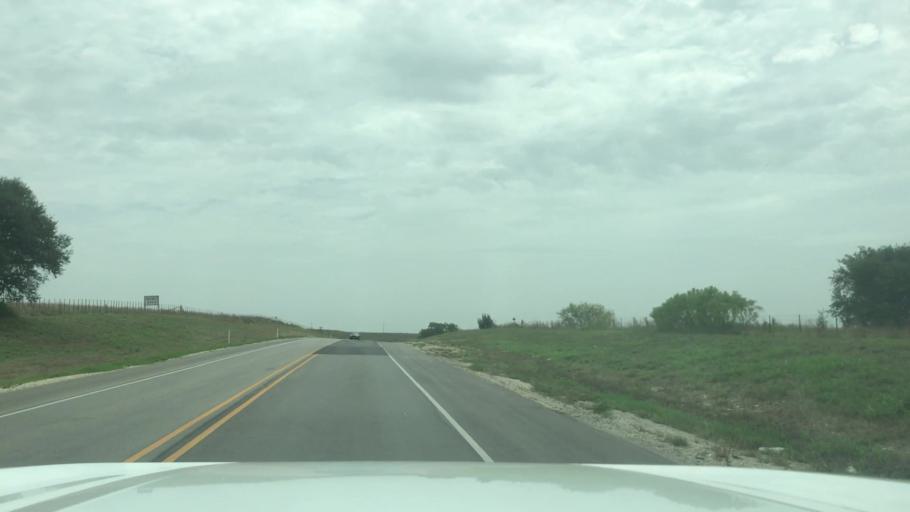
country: US
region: Texas
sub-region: Erath County
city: Dublin
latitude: 32.0732
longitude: -98.2259
